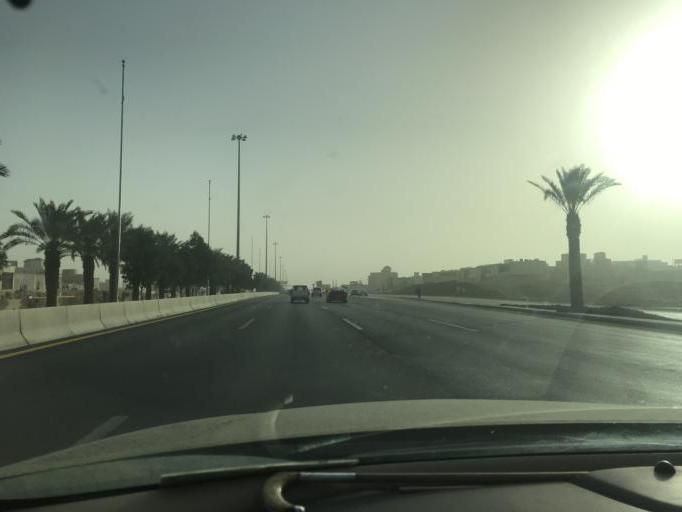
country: SA
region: Ar Riyad
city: Riyadh
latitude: 24.8507
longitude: 46.6718
